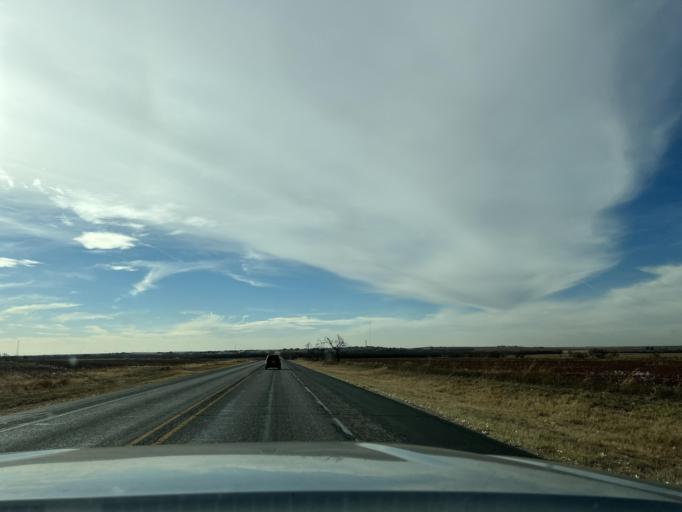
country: US
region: Texas
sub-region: Fisher County
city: Roby
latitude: 32.7506
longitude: -100.3501
